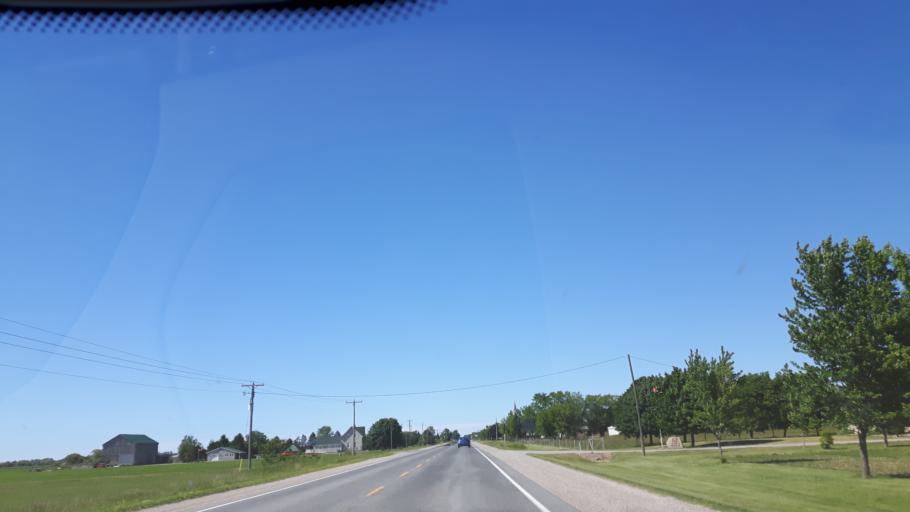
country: CA
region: Ontario
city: Bluewater
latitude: 43.4326
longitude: -81.7036
